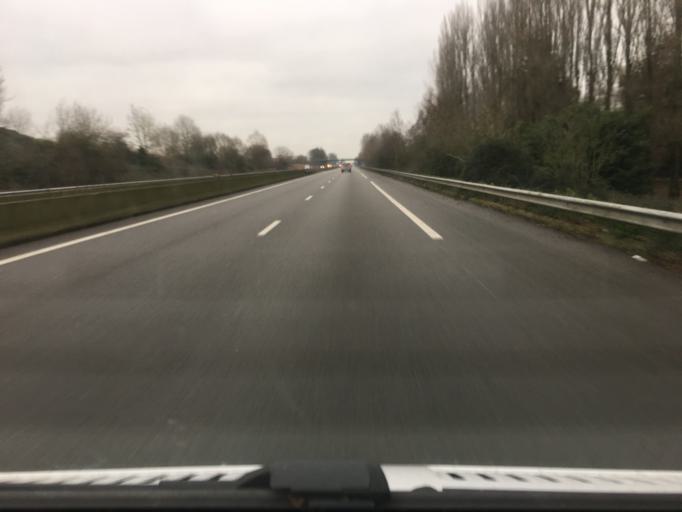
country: FR
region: Nord-Pas-de-Calais
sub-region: Departement du Nord
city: Winnezeele
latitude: 50.8499
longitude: 2.5562
